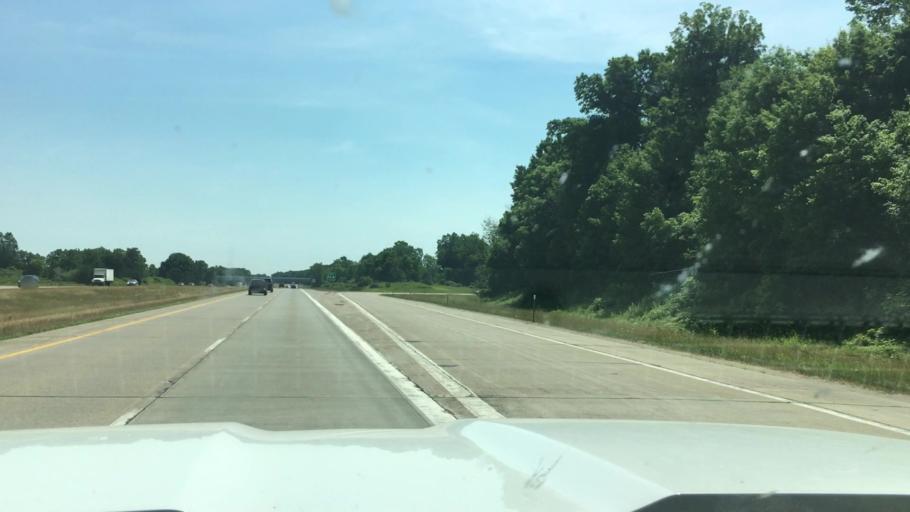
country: US
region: Michigan
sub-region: Clinton County
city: DeWitt
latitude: 42.8073
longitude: -84.6108
